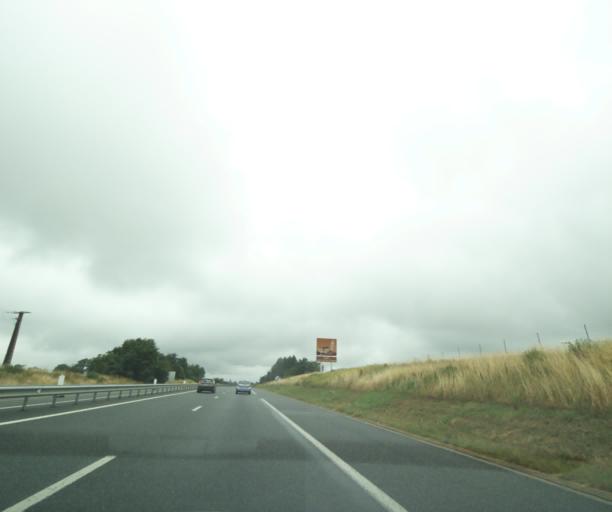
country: FR
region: Midi-Pyrenees
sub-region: Departement de l'Aveyron
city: Luc-la-Primaube
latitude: 44.2962
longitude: 2.5223
